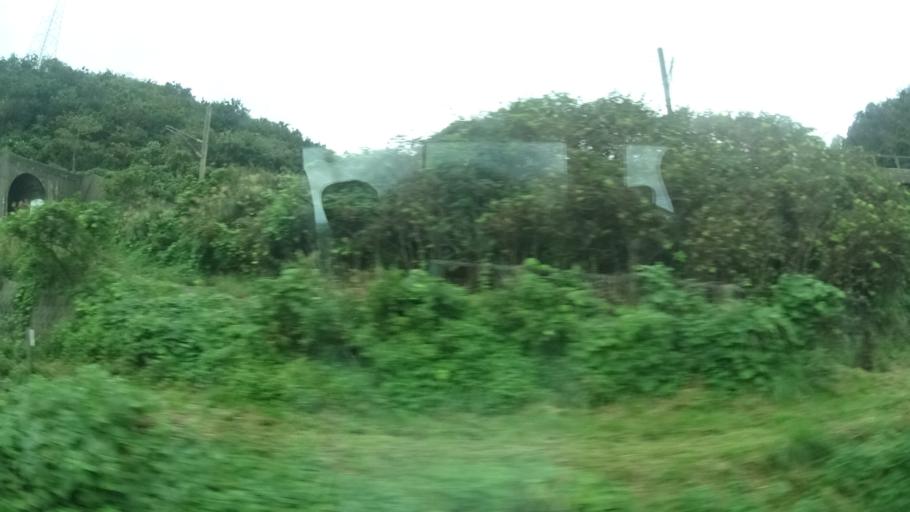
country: JP
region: Niigata
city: Murakami
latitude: 38.5422
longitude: 139.5511
